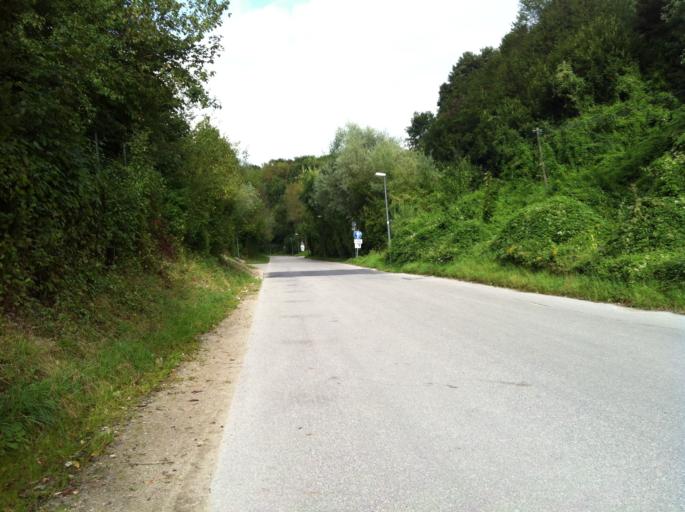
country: DE
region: Bavaria
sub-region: Upper Bavaria
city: Unterfoehring
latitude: 48.2111
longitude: 11.6326
